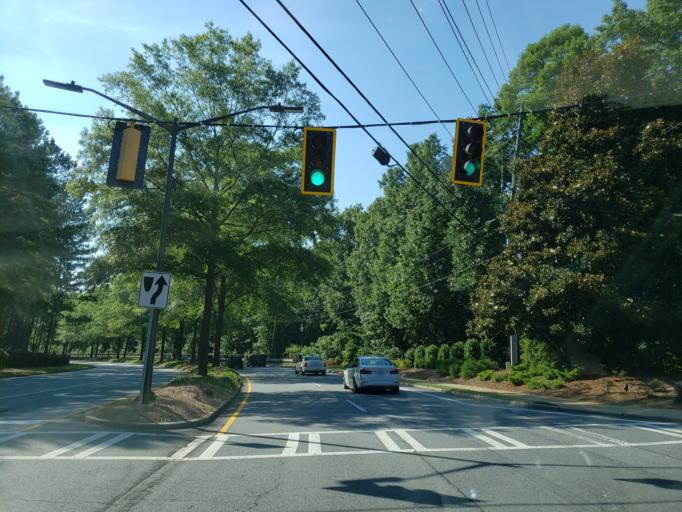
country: US
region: Georgia
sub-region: Cherokee County
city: Woodstock
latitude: 34.1305
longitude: -84.5604
